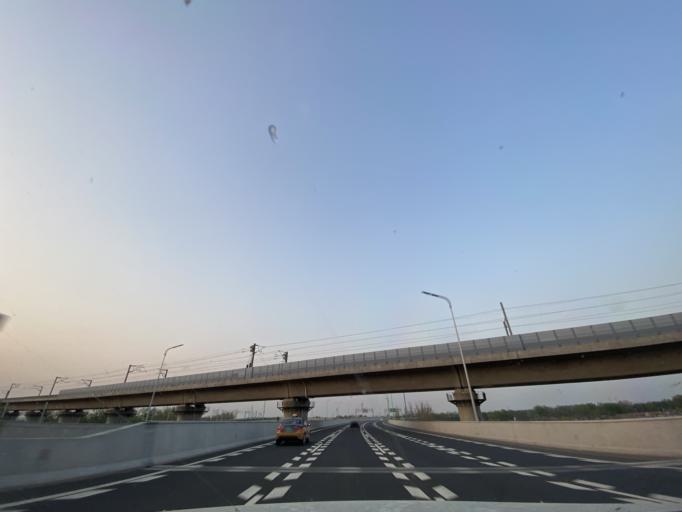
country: CN
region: Beijing
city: Xingfeng
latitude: 39.6852
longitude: 116.3634
